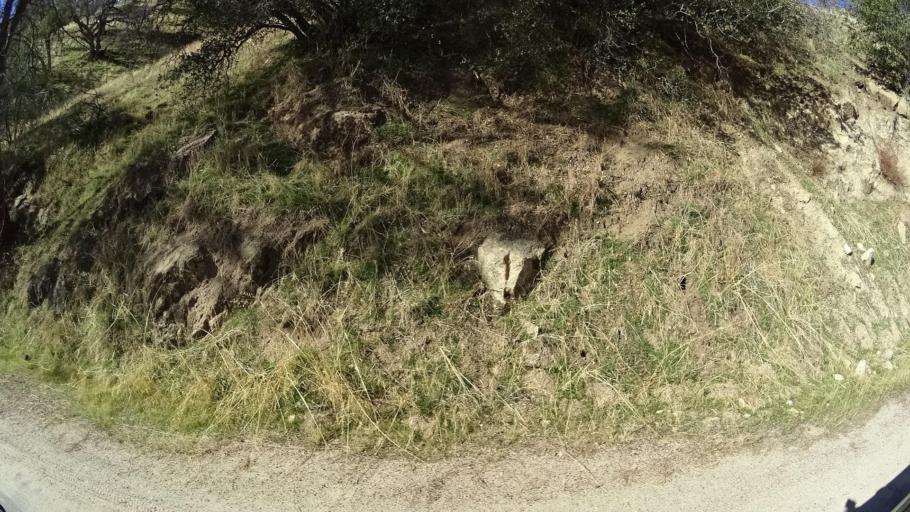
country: US
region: California
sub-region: Kern County
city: Alta Sierra
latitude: 35.6304
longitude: -118.7581
